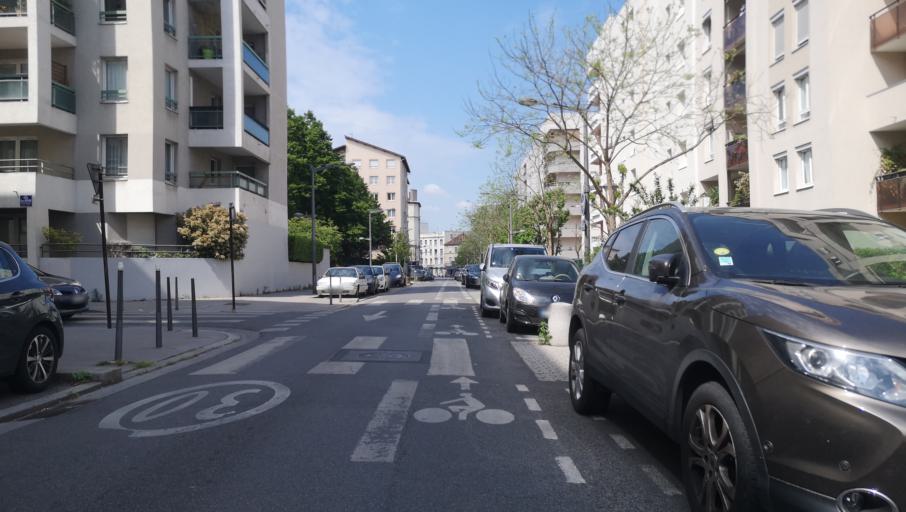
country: FR
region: Rhone-Alpes
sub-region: Departement du Rhone
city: Villeurbanne
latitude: 45.7510
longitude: 4.8686
